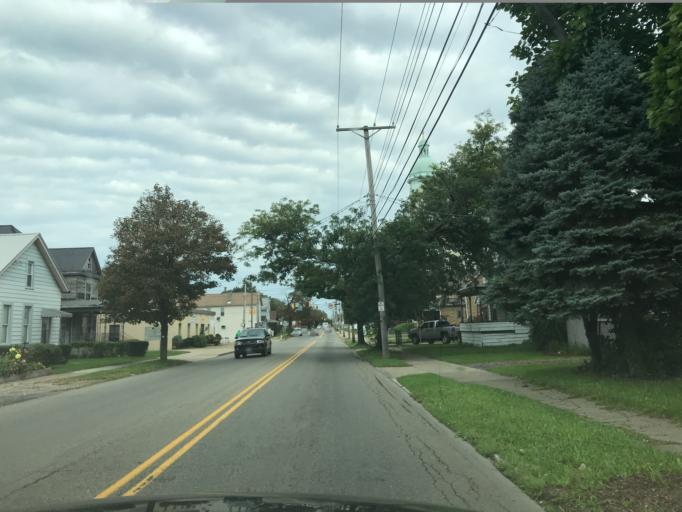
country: US
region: Pennsylvania
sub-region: Erie County
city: Erie
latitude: 42.1155
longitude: -80.0637
